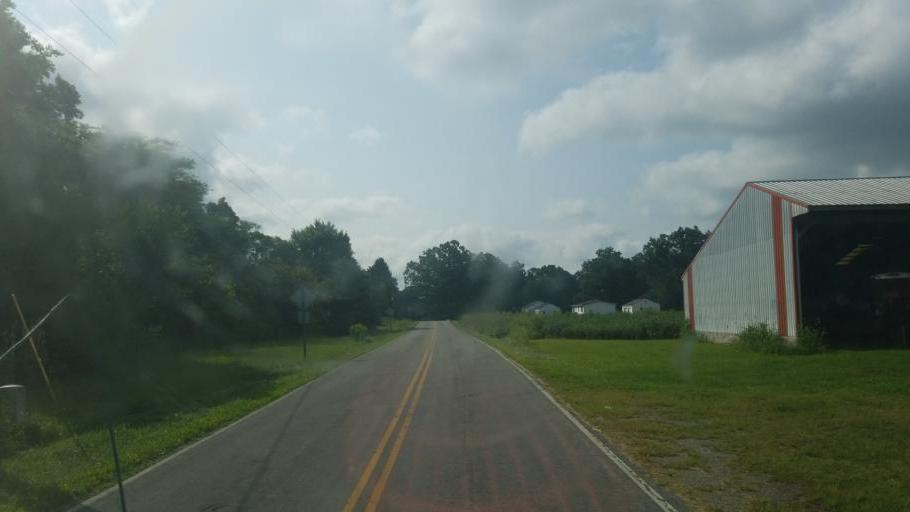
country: US
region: Ohio
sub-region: Morrow County
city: Cardington
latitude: 40.5752
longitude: -82.9983
